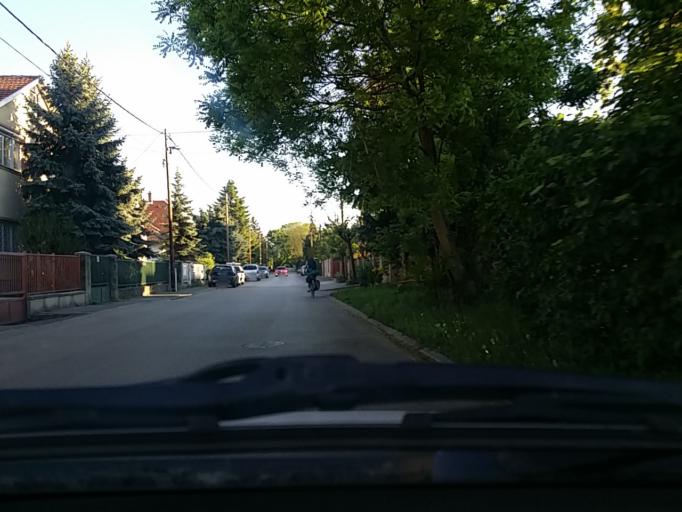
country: HU
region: Pest
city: Budakalasz
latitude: 47.5921
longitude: 19.0587
